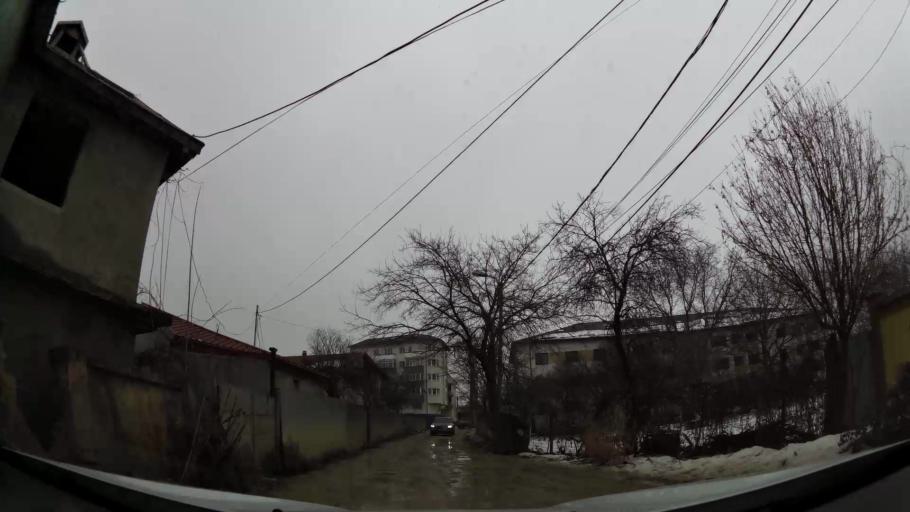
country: RO
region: Ilfov
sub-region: Comuna Popesti-Leordeni
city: Popesti-Leordeni
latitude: 44.4059
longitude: 26.1658
